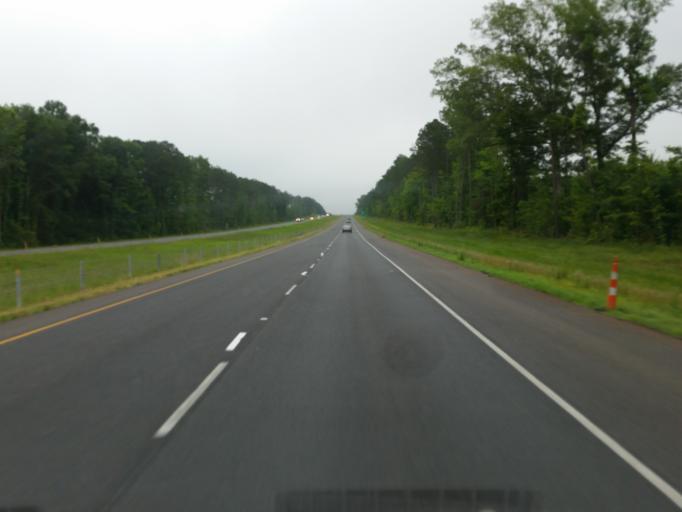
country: US
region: Louisiana
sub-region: Bienville Parish
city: Arcadia
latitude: 32.5633
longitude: -93.0826
